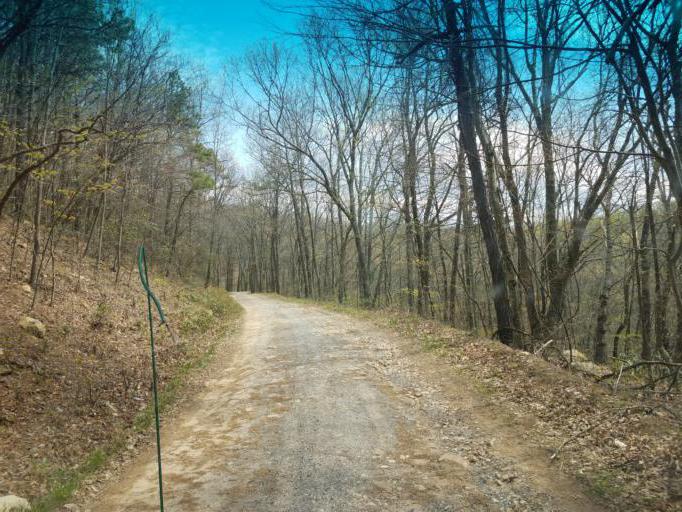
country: US
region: Virginia
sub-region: Smyth County
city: Marion
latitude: 36.7905
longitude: -81.4713
